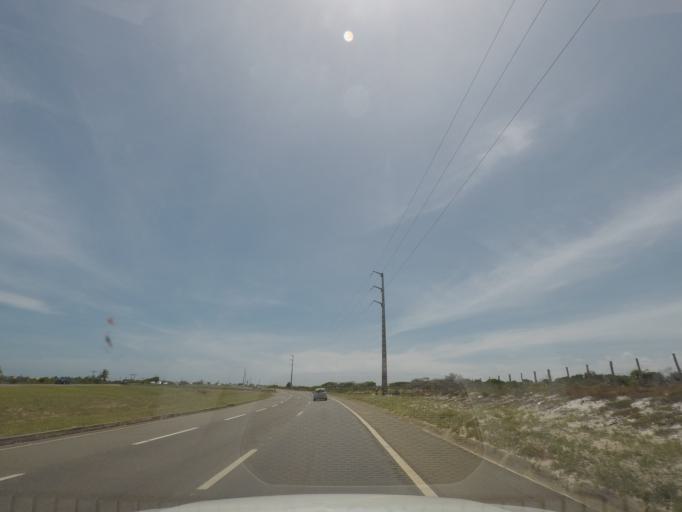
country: BR
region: Bahia
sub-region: Camacari
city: Camacari
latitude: -12.6761
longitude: -38.1026
